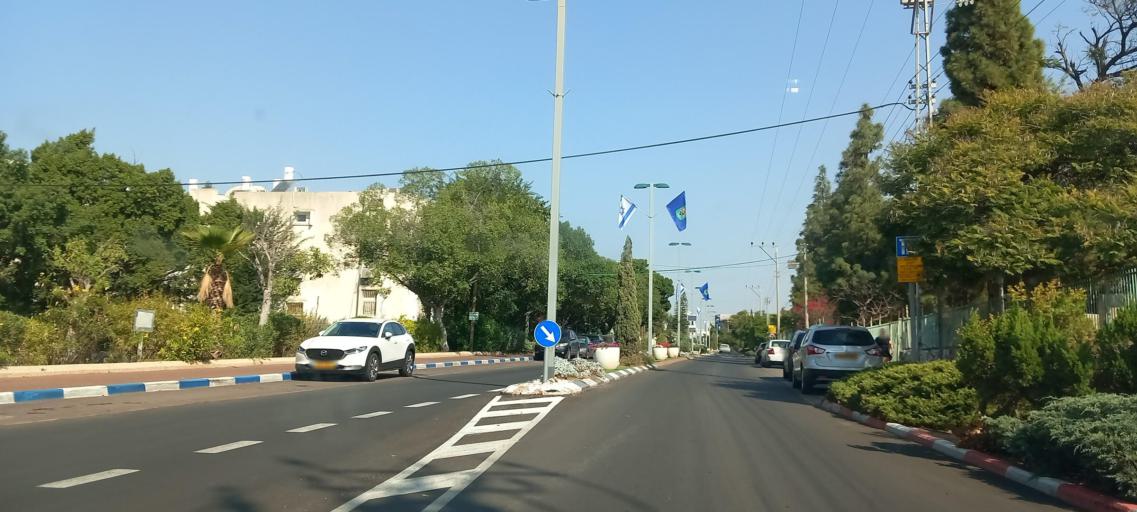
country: IL
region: Tel Aviv
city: Or Yehuda
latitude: 32.0490
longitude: 34.8363
